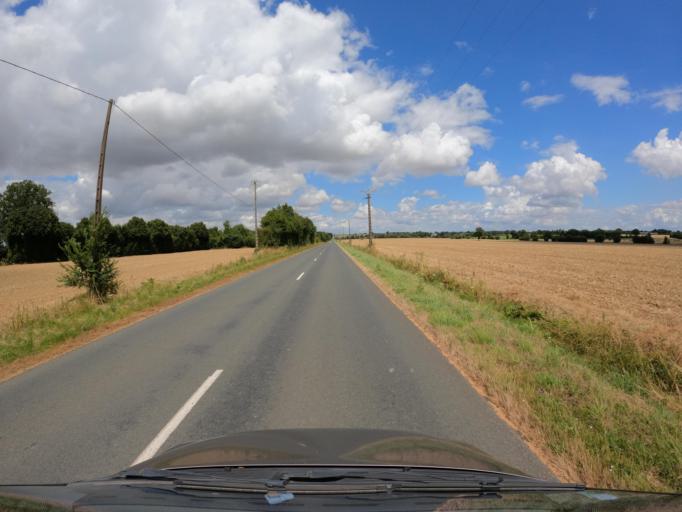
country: FR
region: Pays de la Loire
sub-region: Departement de Maine-et-Loire
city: Mire
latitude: 47.7351
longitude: -0.5127
